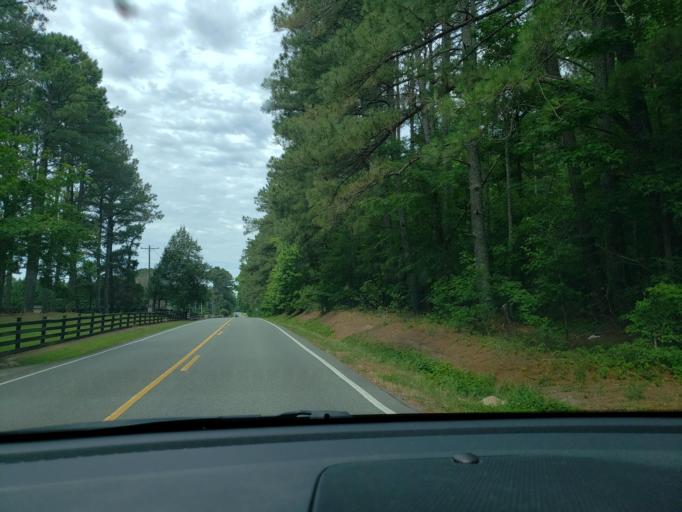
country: US
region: North Carolina
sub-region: Wake County
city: Green Level
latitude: 35.7951
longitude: -78.9823
